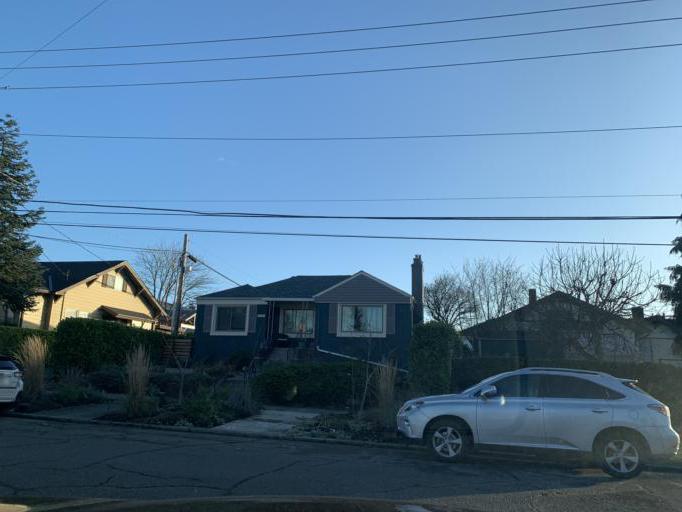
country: US
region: Washington
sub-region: King County
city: Seattle
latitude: 47.5752
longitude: -122.3121
